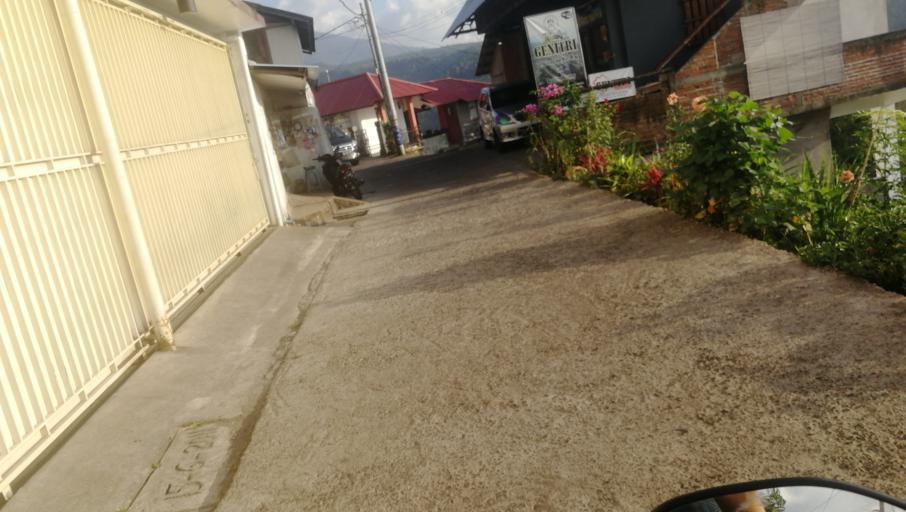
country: ID
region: Bali
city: Munduk
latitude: -8.2669
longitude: 115.0546
